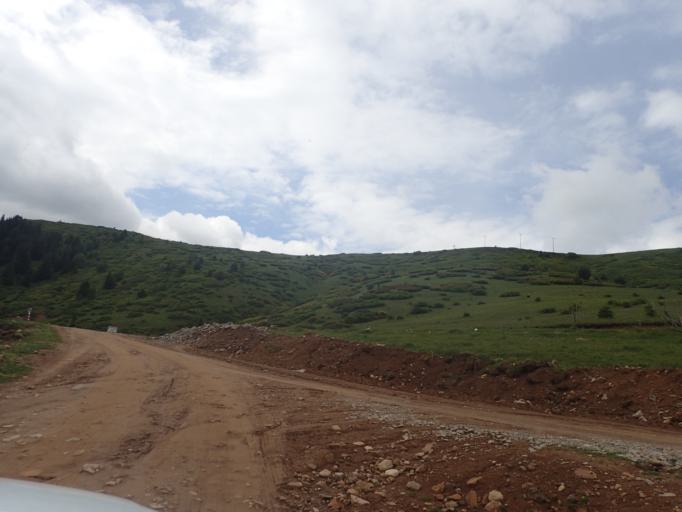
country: TR
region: Ordu
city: Yesilce
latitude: 40.6100
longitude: 37.9666
